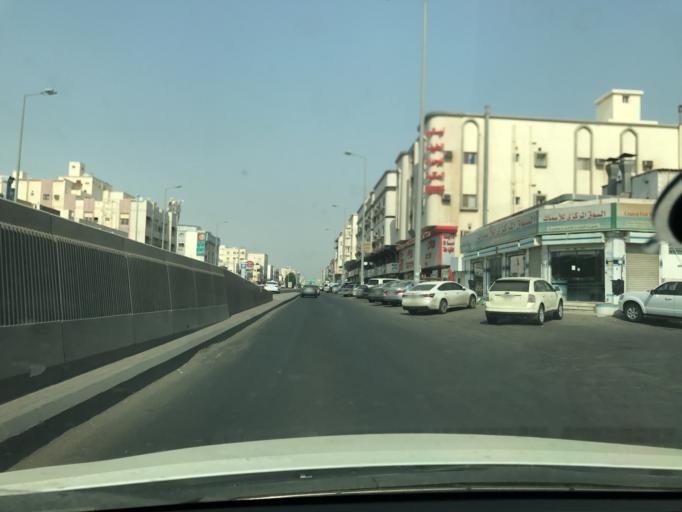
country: SA
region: Makkah
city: Jeddah
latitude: 21.6200
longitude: 39.1882
